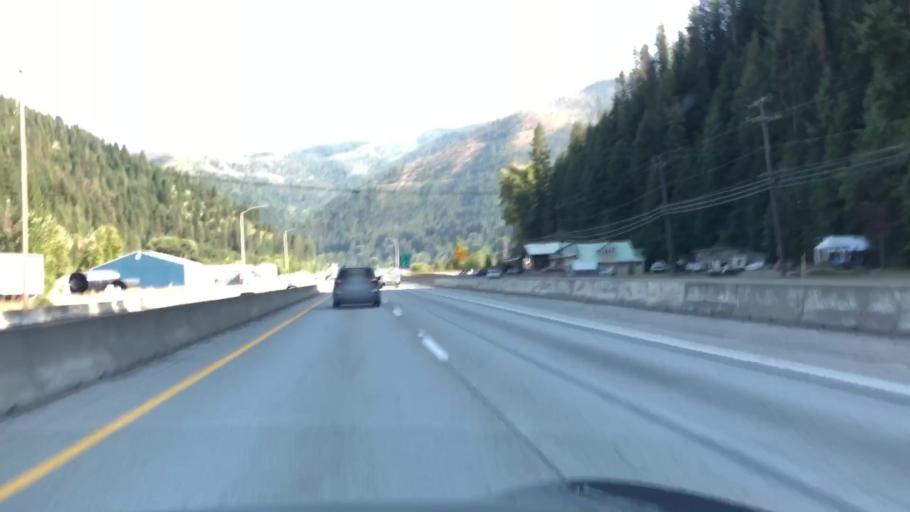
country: US
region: Idaho
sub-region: Shoshone County
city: Wallace
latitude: 47.4823
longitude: -115.9388
